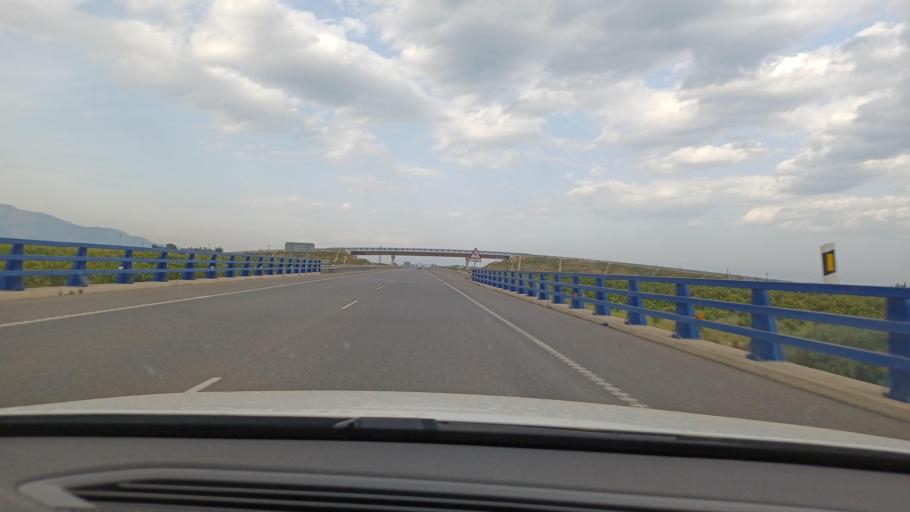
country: ES
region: Valencia
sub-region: Provincia de Castello
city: Vinaros
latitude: 40.5037
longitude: 0.4738
